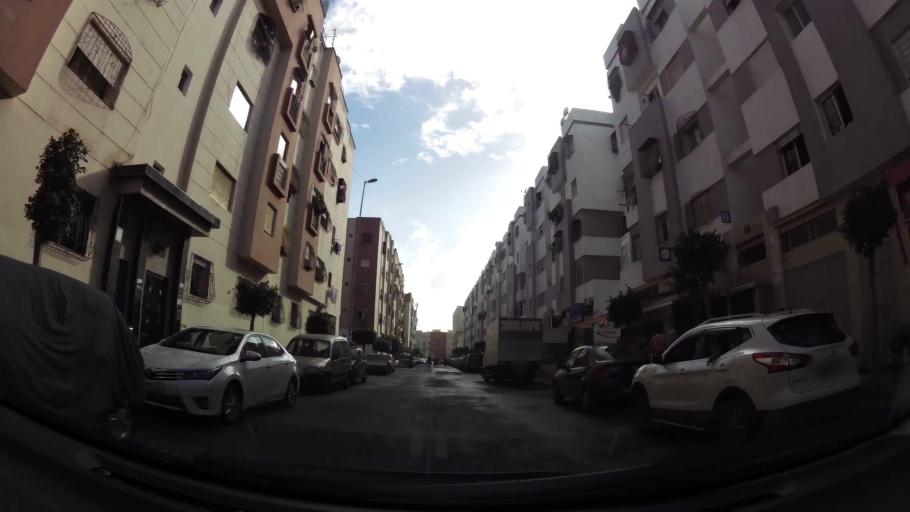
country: MA
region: Grand Casablanca
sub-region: Casablanca
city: Casablanca
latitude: 33.5555
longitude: -7.6990
